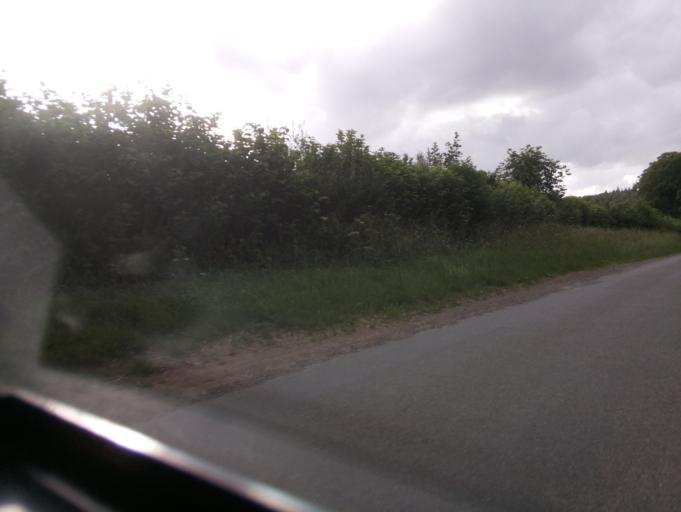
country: GB
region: England
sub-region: Gloucestershire
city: Donnington
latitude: 51.9741
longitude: -1.7533
